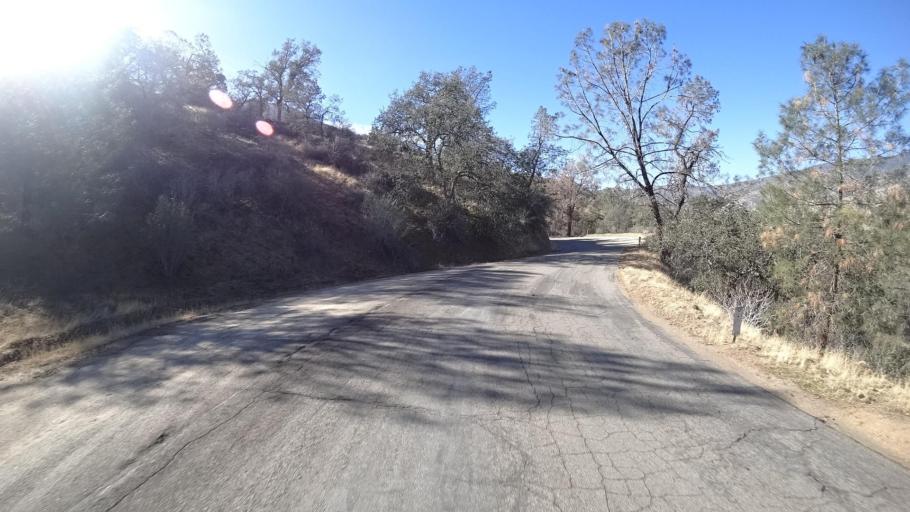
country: US
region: California
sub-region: Kern County
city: Bodfish
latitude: 35.5309
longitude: -118.6251
